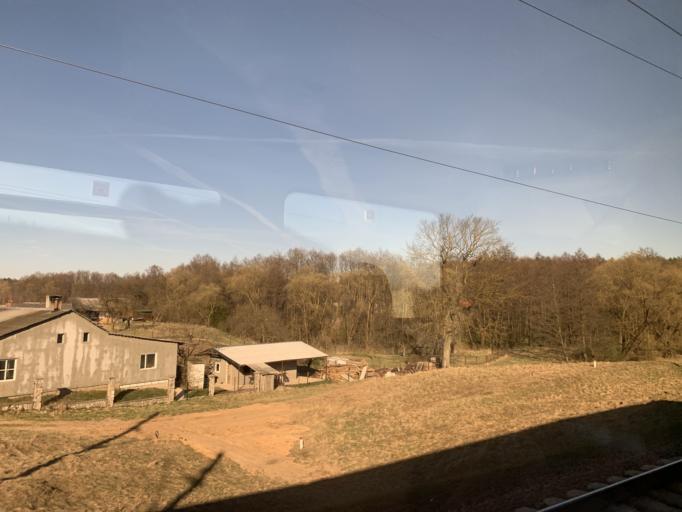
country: BY
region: Grodnenskaya
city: Smarhon'
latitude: 54.4321
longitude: 26.5218
